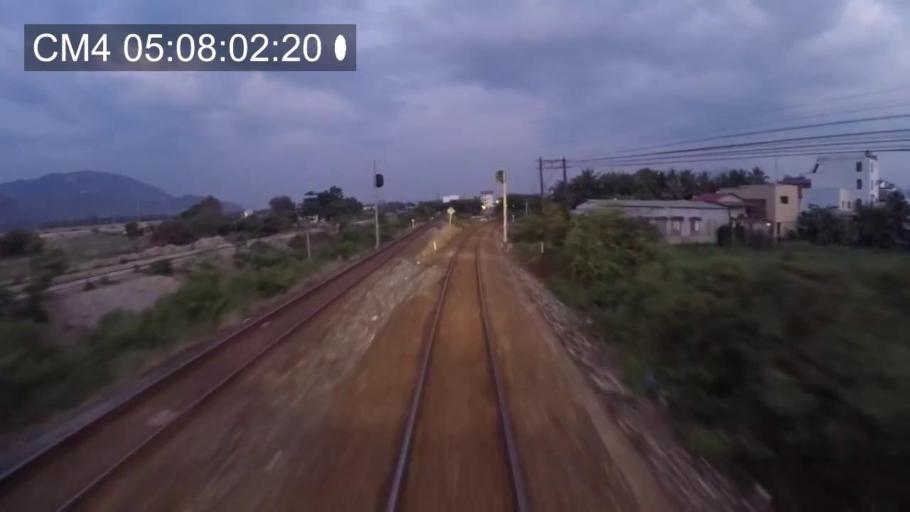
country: VN
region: Khanh Hoa
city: Nha Trang
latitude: 12.2894
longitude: 109.1861
